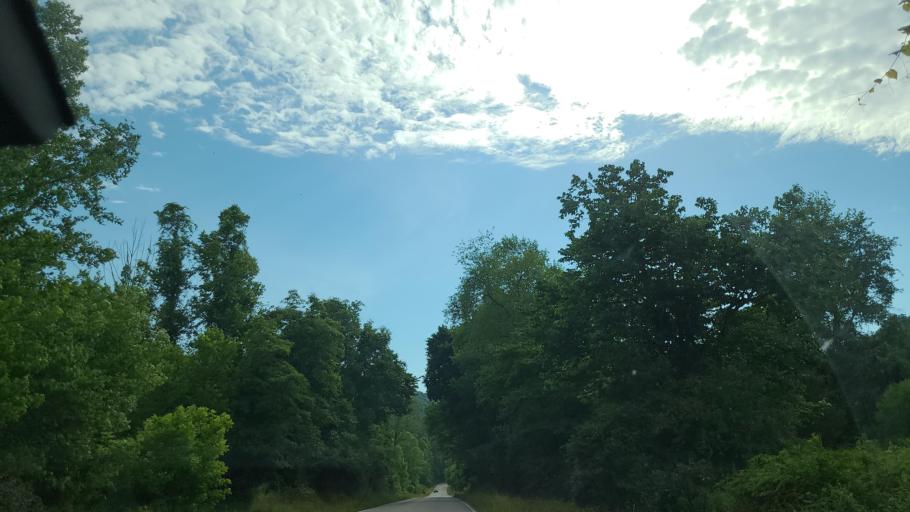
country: US
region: Kentucky
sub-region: Knox County
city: Barbourville
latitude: 36.6799
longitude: -83.9301
